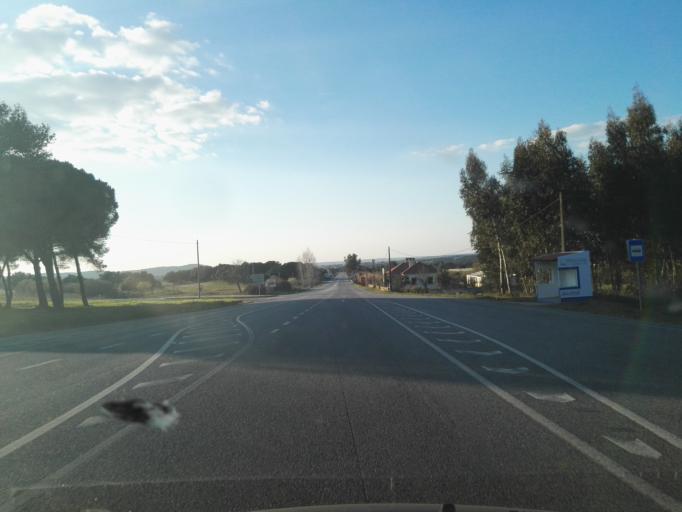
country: PT
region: Evora
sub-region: Arraiolos
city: Arraiolos
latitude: 38.6046
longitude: -8.0524
